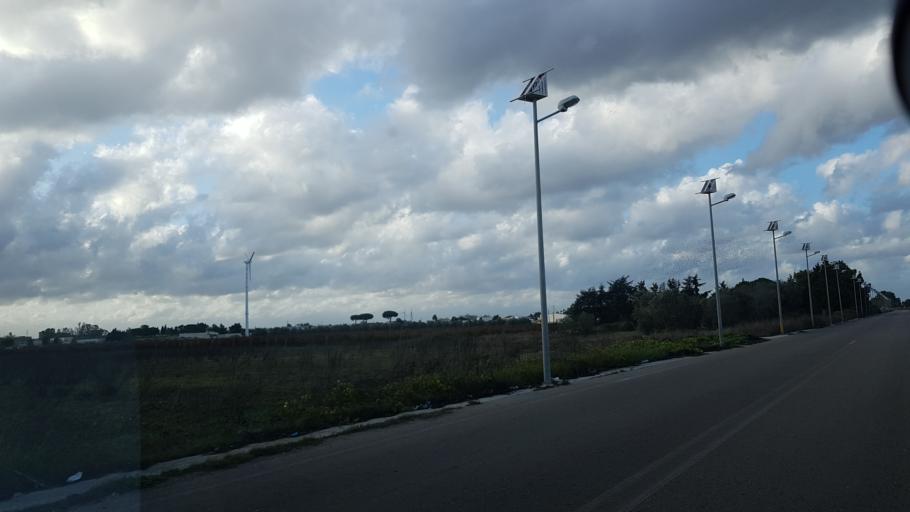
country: IT
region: Apulia
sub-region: Provincia di Brindisi
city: San Pietro Vernotico
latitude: 40.4928
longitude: 18.0094
